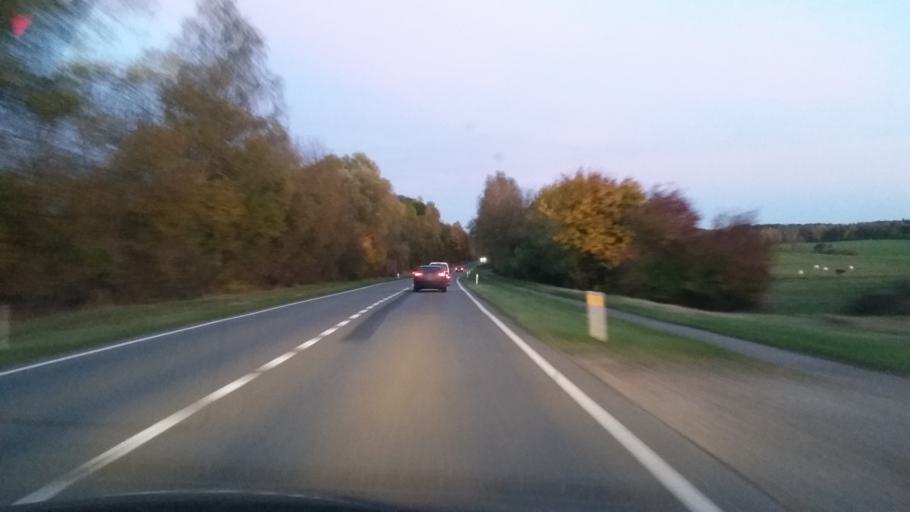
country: BE
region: Wallonia
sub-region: Province du Luxembourg
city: Etalle
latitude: 49.6756
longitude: 5.6212
